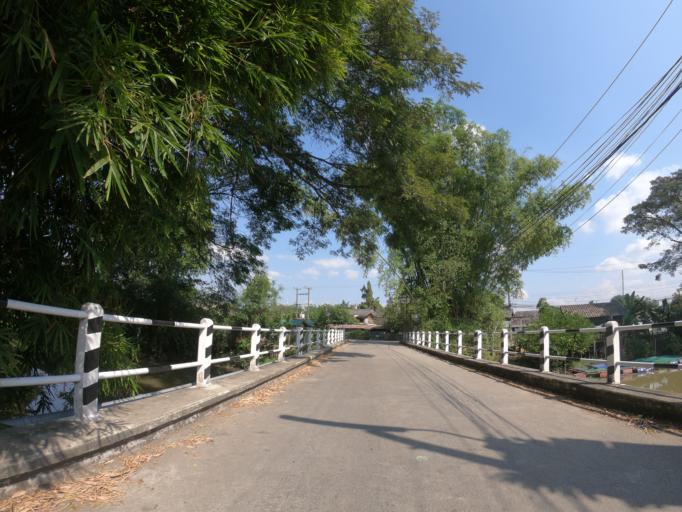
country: TH
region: Chiang Mai
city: Chiang Mai
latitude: 18.8057
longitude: 99.0268
